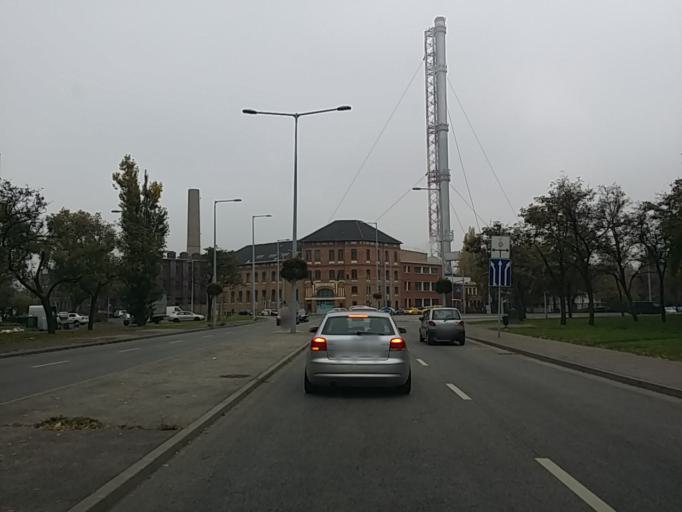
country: HU
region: Budapest
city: Budapest IV. keruelet
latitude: 47.5560
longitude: 19.1013
